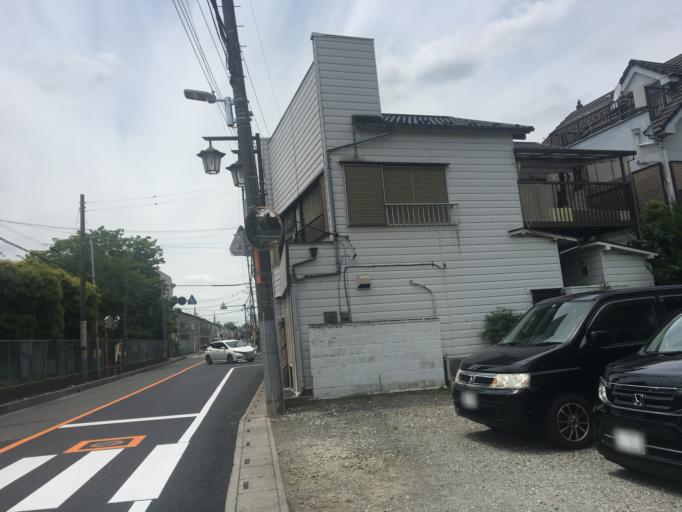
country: JP
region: Saitama
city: Shimotoda
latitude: 35.8288
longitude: 139.6729
